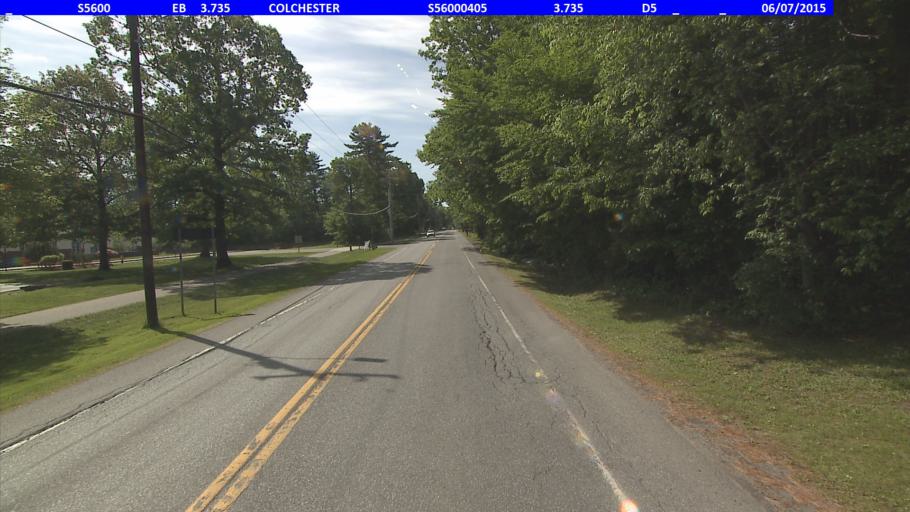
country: US
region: Vermont
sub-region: Chittenden County
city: Winooski
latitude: 44.5385
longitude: -73.2091
